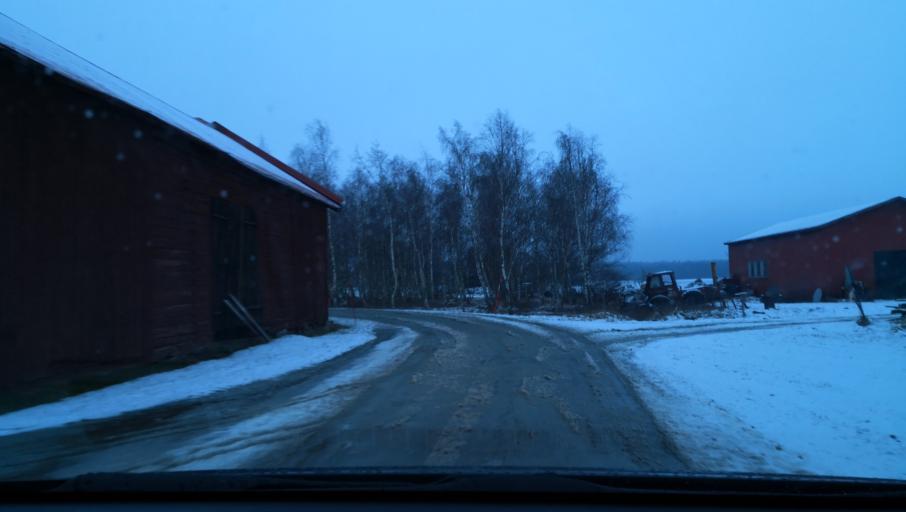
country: SE
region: Vaestmanland
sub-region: Kungsors Kommun
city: Kungsoer
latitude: 59.3940
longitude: 16.2126
